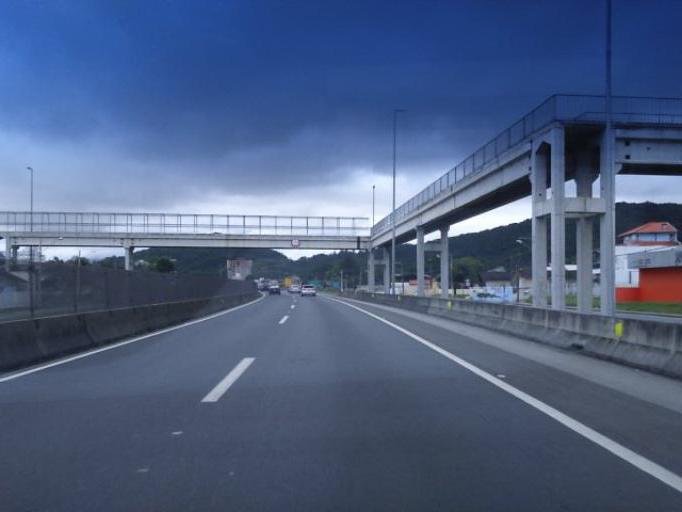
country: BR
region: Santa Catarina
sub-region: Itapema
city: Itapema
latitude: -27.0990
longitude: -48.6186
